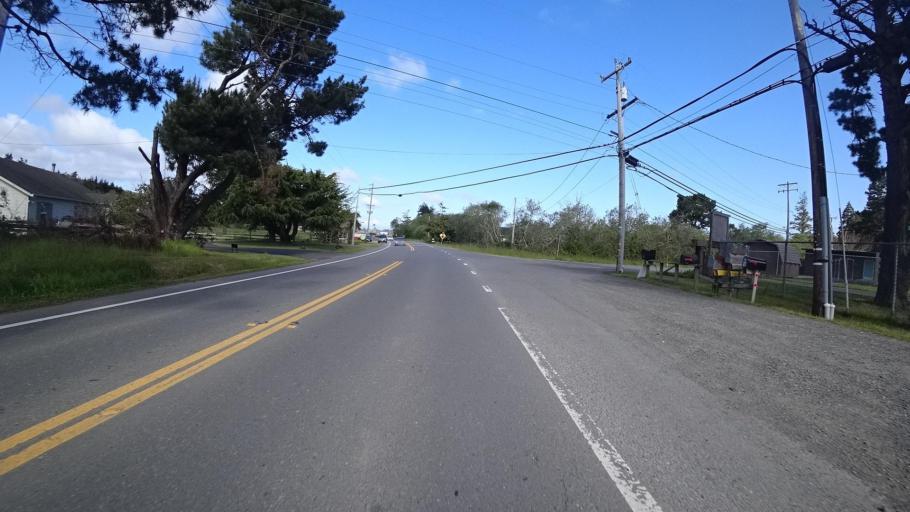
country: US
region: California
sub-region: Humboldt County
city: Myrtletown
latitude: 40.7849
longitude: -124.0830
